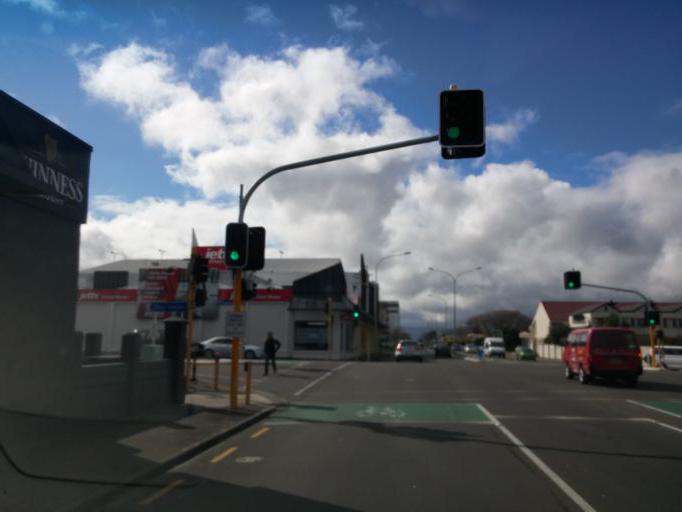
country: NZ
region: Manawatu-Wanganui
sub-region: Palmerston North City
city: Palmerston North
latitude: -40.3595
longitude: 175.6130
